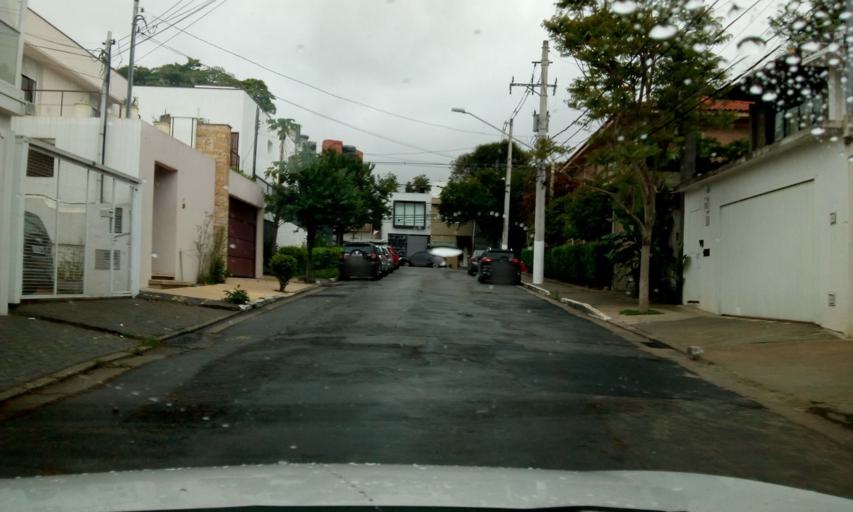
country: BR
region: Sao Paulo
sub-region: Sao Paulo
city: Sao Paulo
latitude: -23.5880
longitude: -46.6676
